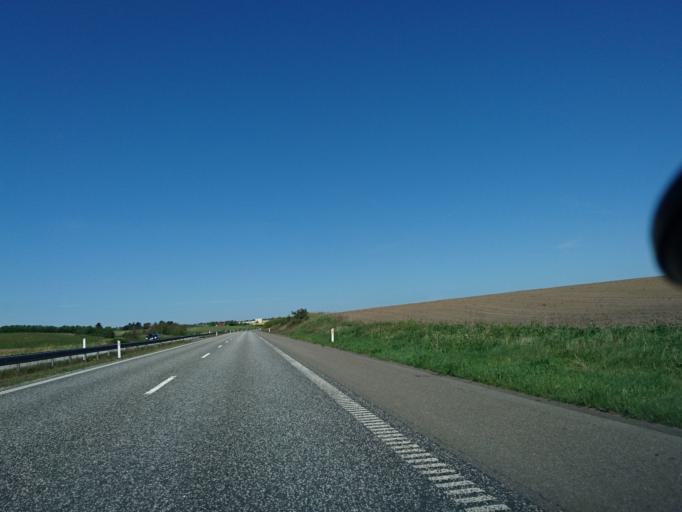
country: DK
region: North Denmark
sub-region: Hjorring Kommune
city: Hirtshals
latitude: 57.5339
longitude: 10.0104
